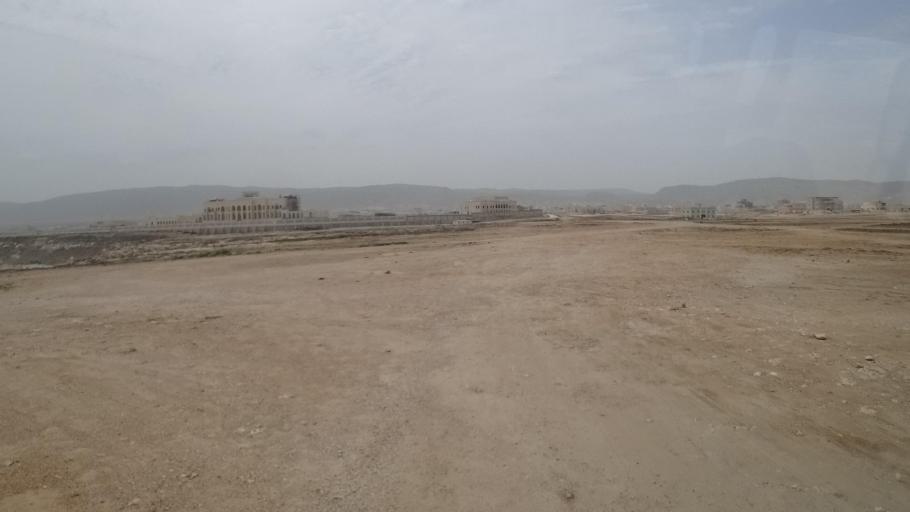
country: OM
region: Zufar
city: Salalah
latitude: 17.0350
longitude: 54.4092
